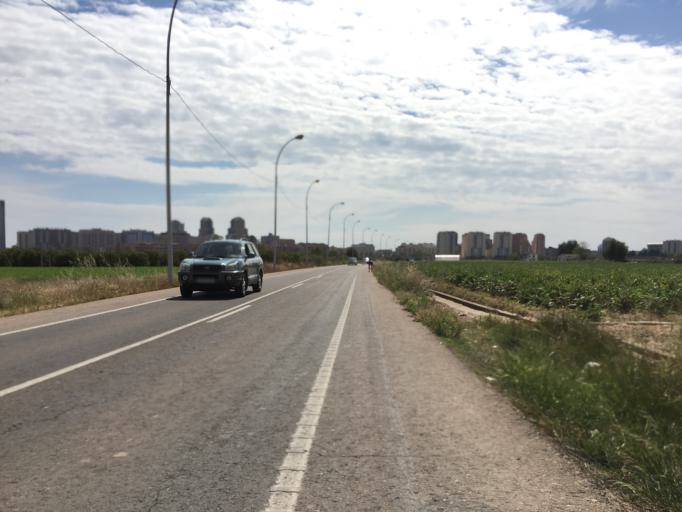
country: ES
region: Valencia
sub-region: Provincia de Valencia
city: Mislata
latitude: 39.4905
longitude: -0.4164
